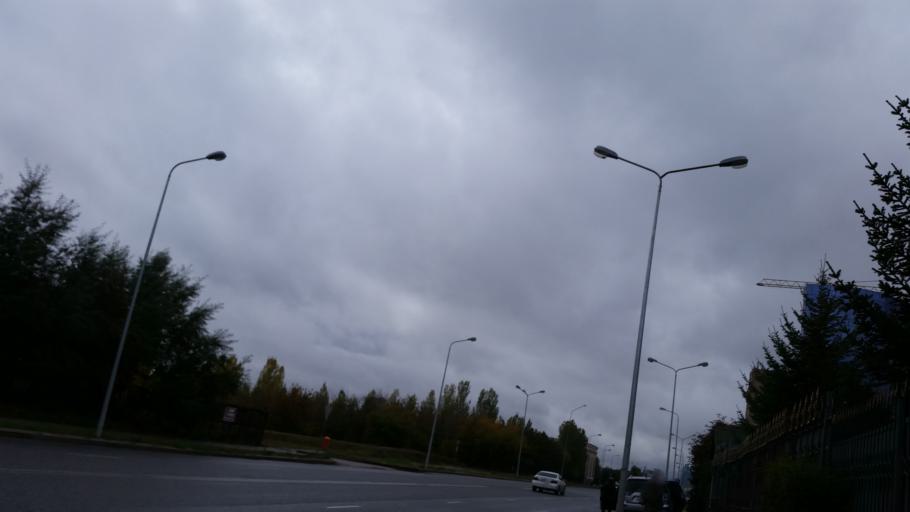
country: KZ
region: Astana Qalasy
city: Astana
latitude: 51.1489
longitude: 71.4882
